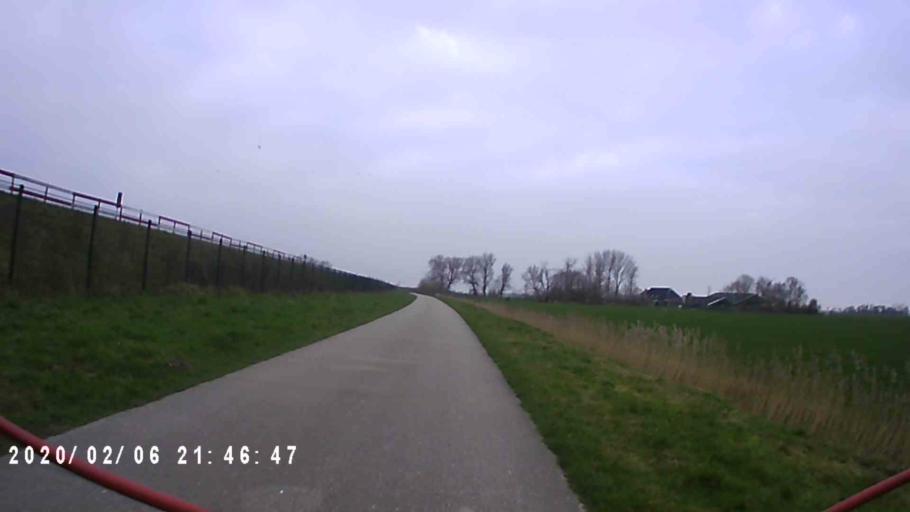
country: NL
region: Groningen
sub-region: Gemeente Zuidhorn
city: Noordhorn
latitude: 53.2552
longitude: 6.3822
